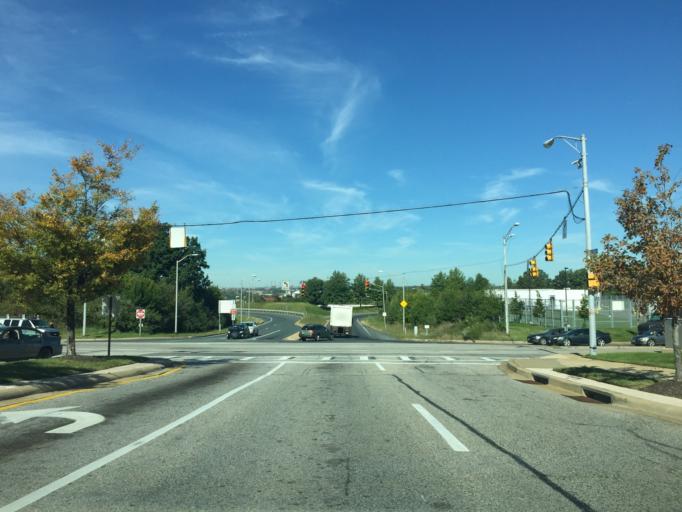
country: US
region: Maryland
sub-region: Baltimore County
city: Rosedale
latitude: 39.2921
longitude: -76.5508
